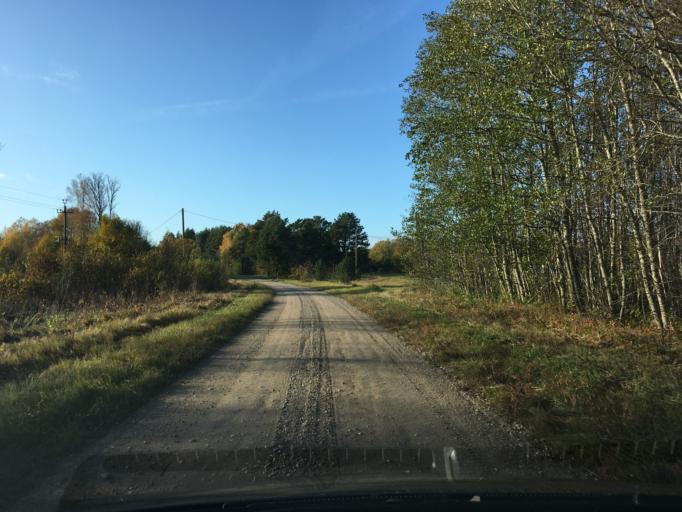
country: EE
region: Laeaene
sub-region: Lihula vald
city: Lihula
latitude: 58.5671
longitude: 23.7639
